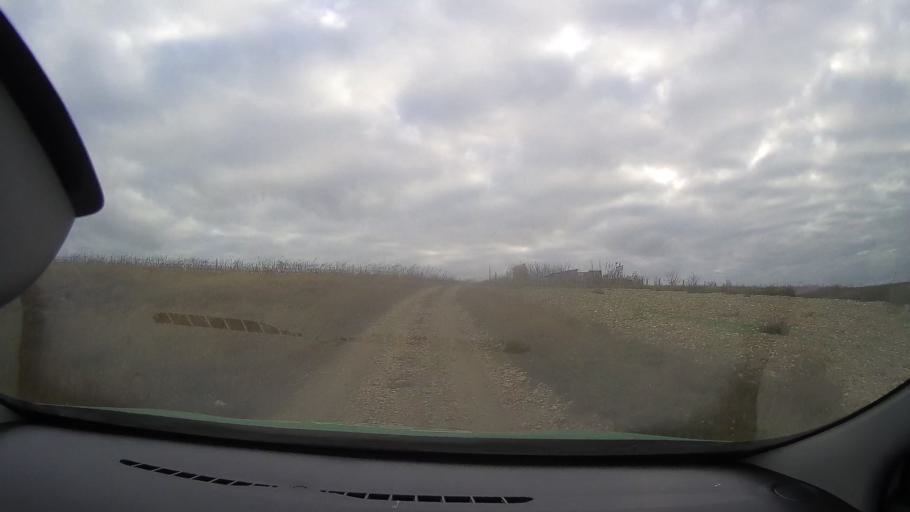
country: RO
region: Tulcea
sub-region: Comuna Jurilovca
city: Jurilovca
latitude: 44.7682
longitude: 28.9165
